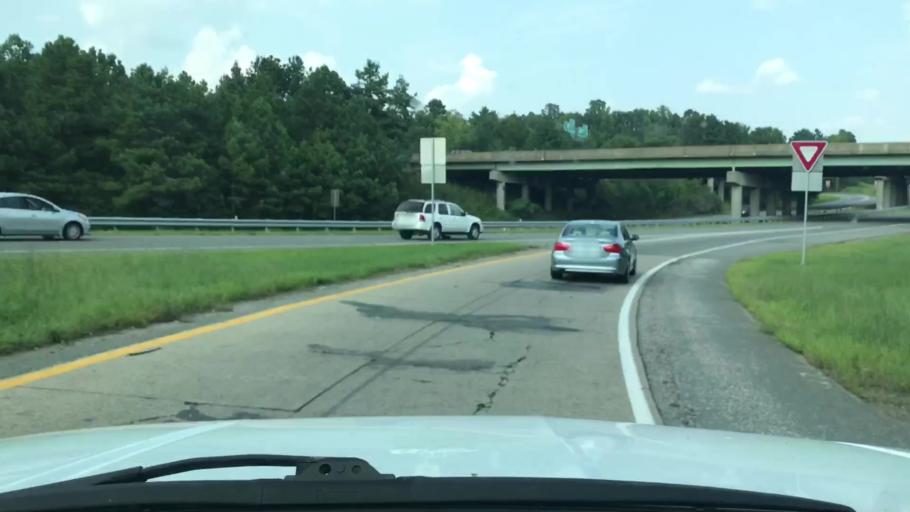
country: US
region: Virginia
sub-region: Hanover County
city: Mechanicsville
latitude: 37.6069
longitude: -77.3622
